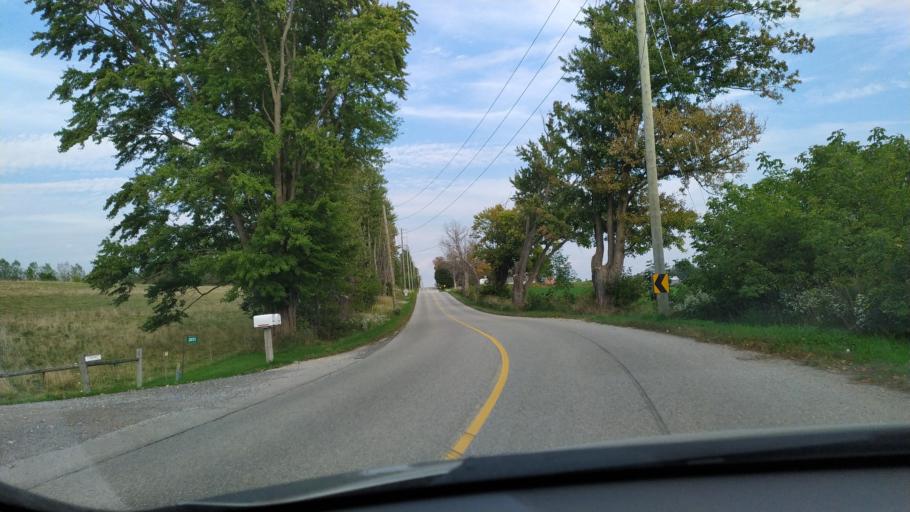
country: CA
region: Ontario
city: Stratford
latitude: 43.4689
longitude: -80.7822
